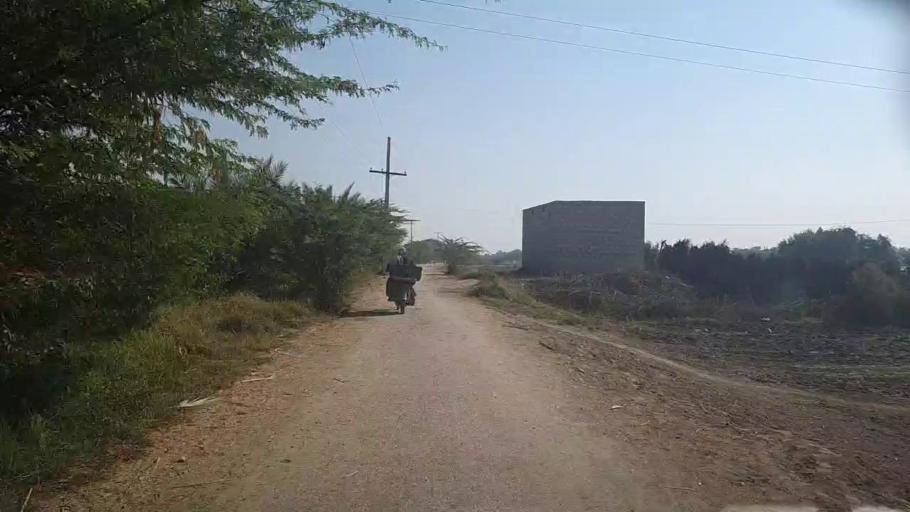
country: PK
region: Sindh
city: Kot Diji
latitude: 27.4379
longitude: 68.7113
